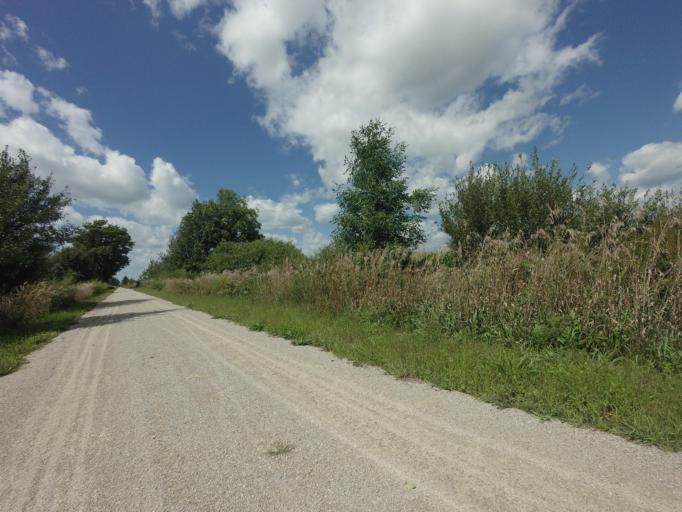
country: CA
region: Ontario
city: Huron East
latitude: 43.6029
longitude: -81.1124
